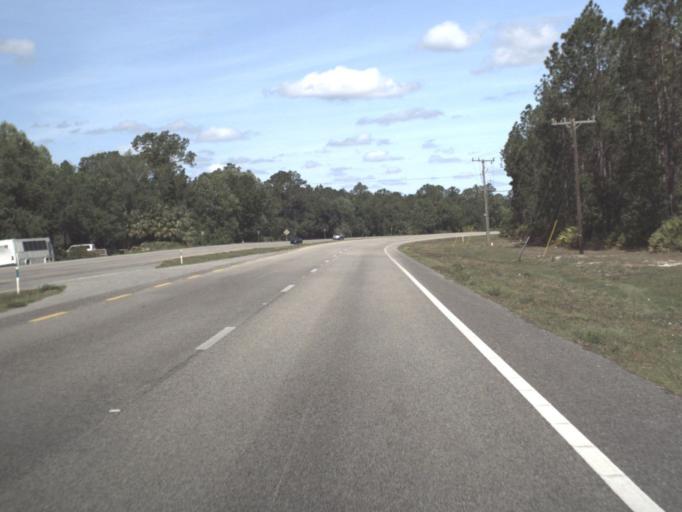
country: US
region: Florida
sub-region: Flagler County
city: Bunnell
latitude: 29.4314
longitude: -81.2296
